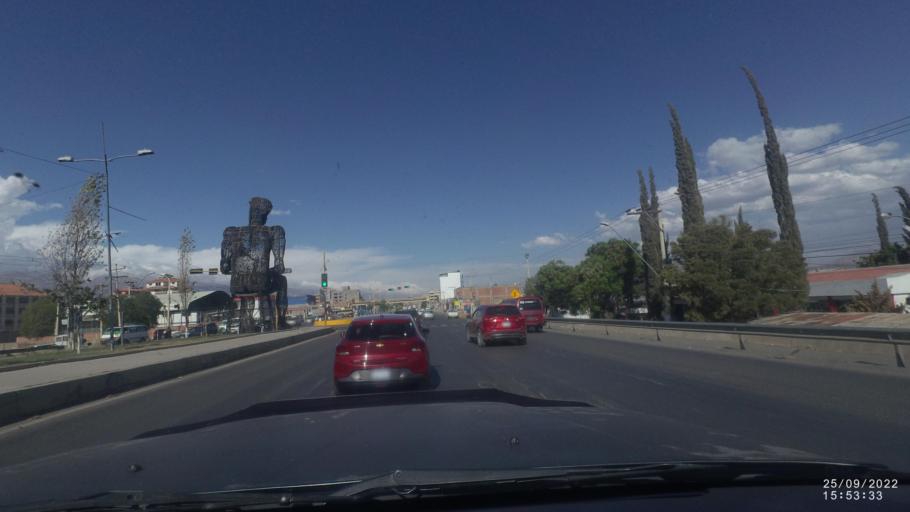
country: BO
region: Cochabamba
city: Sipe Sipe
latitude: -17.3953
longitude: -66.2924
